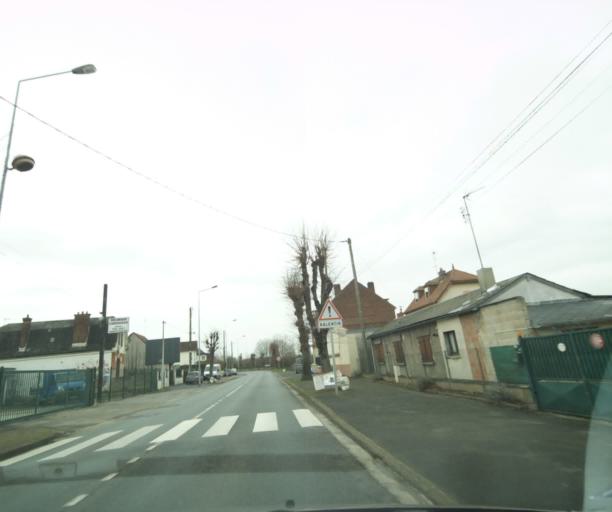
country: FR
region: Picardie
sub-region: Departement de l'Oise
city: Noyon
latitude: 49.5783
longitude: 3.0205
